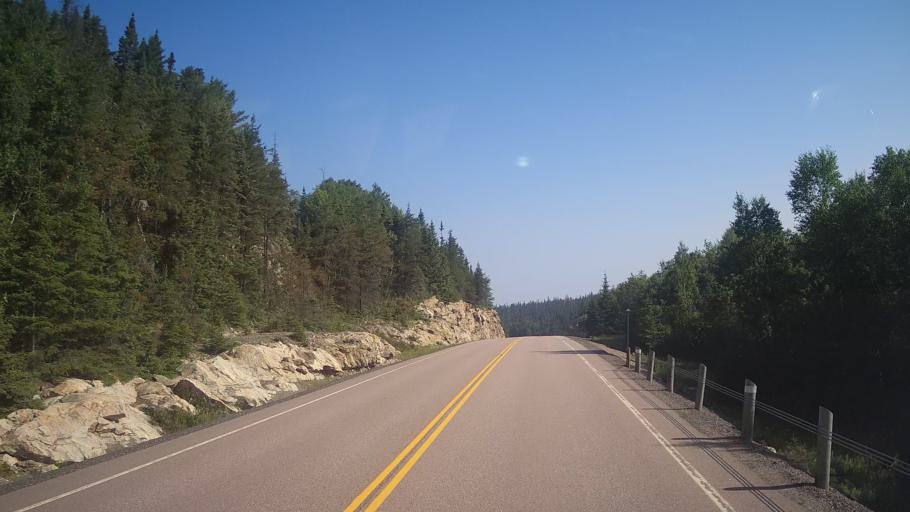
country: CA
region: Ontario
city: Rayside-Balfour
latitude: 46.9917
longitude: -81.6328
